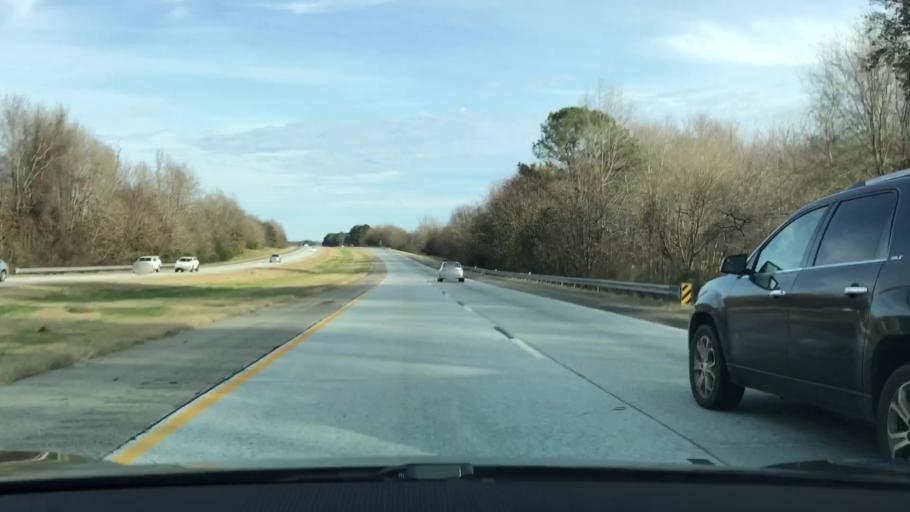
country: US
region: Georgia
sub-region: Morgan County
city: Madison
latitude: 33.5537
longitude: -83.4085
